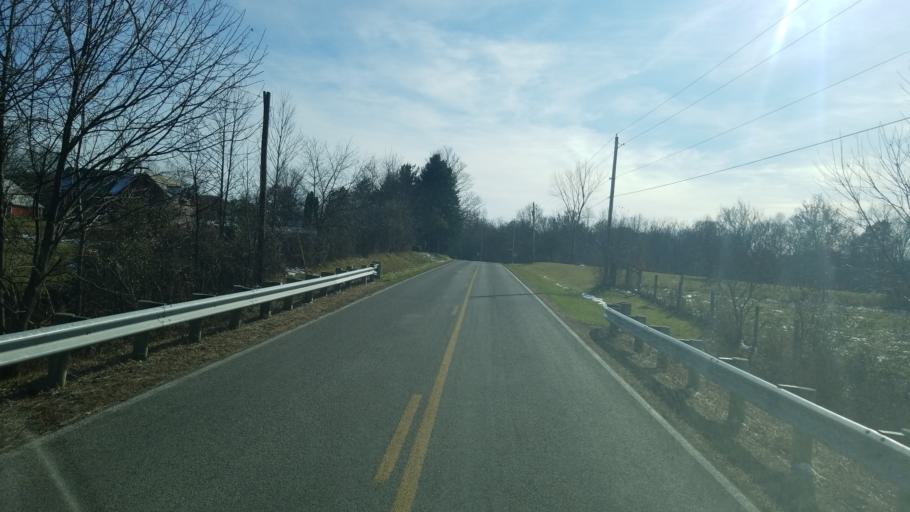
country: US
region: Ohio
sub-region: Lorain County
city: Camden
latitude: 41.1985
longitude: -82.3602
